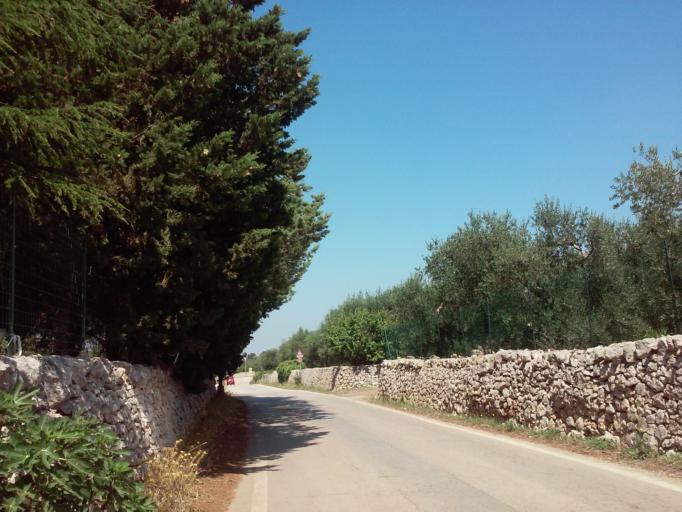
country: IT
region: Apulia
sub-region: Provincia di Bari
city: Alberobello
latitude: 40.7942
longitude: 17.2210
